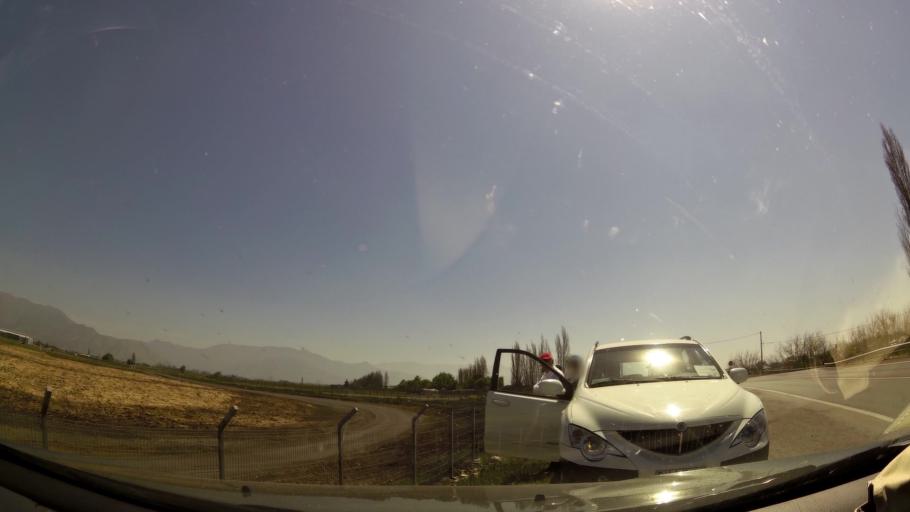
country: CL
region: Santiago Metropolitan
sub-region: Provincia de Santiago
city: Lo Prado
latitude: -33.3732
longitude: -70.7847
